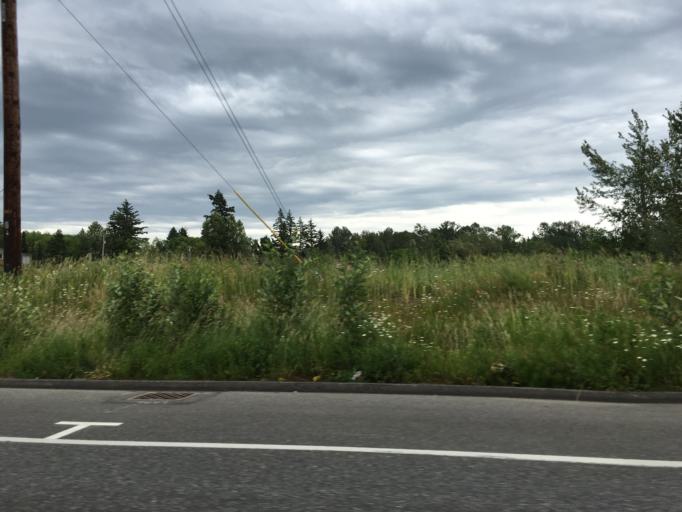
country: US
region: Washington
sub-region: Whatcom County
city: Bellingham
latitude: 48.8071
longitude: -122.4860
